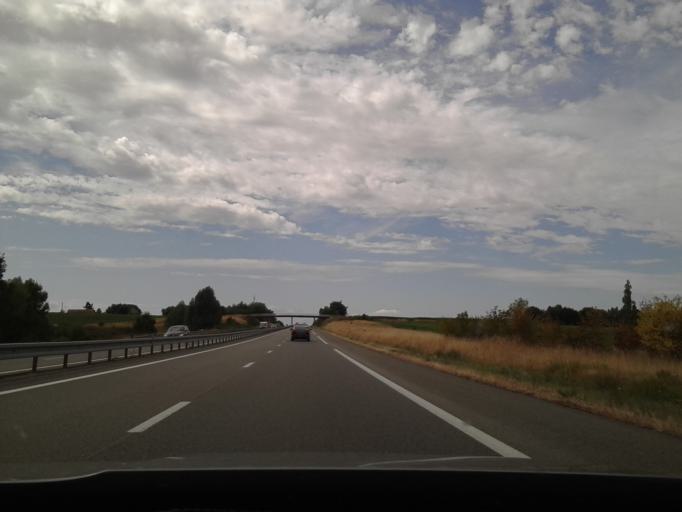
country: FR
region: Pays de la Loire
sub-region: Departement de la Sarthe
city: Sainte-Jamme-sur-Sarthe
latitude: 48.1417
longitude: 0.1435
